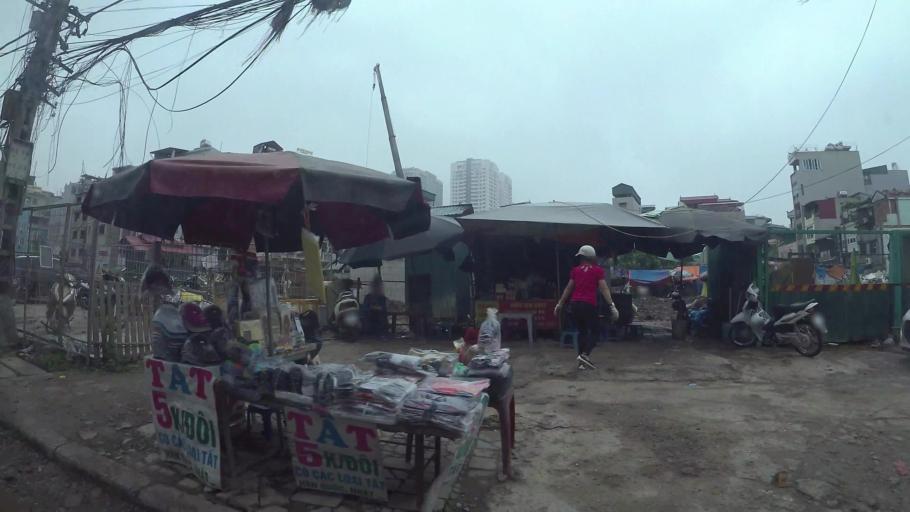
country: VN
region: Ha Noi
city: Dong Da
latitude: 21.0021
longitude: 105.8236
